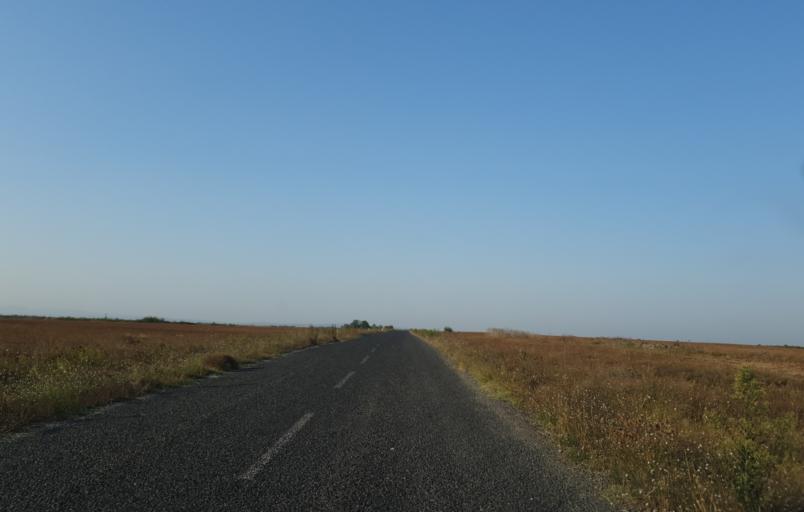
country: TR
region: Tekirdag
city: Beyazkoy
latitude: 41.4062
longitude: 27.7599
